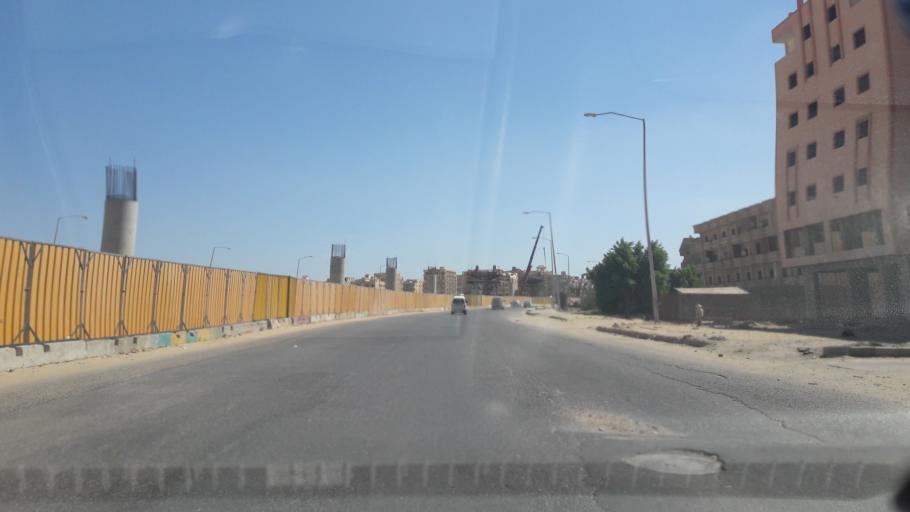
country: EG
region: Al Jizah
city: Madinat Sittah Uktubar
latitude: 29.9671
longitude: 30.9310
